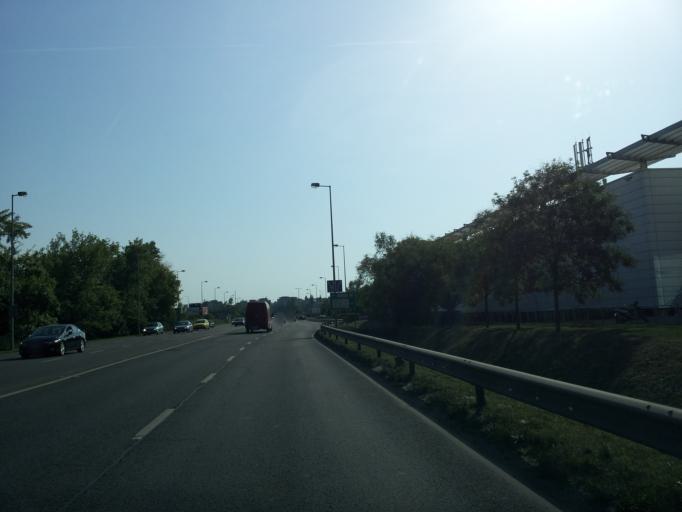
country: HU
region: Budapest
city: Budapest XXII. keruelet
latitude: 47.4354
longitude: 19.0429
